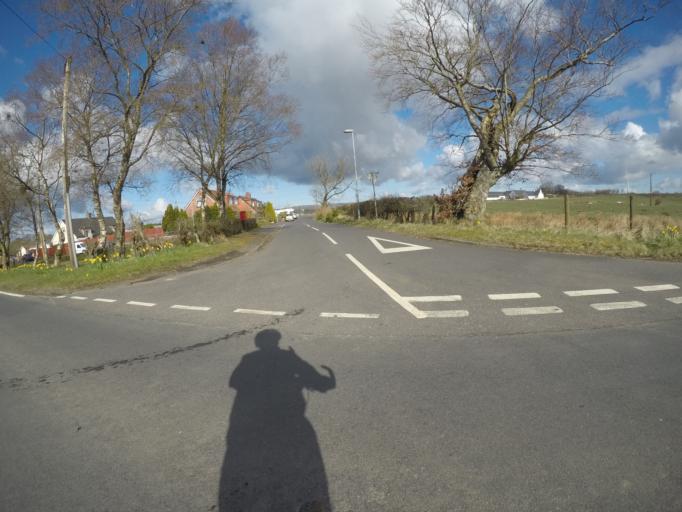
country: GB
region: Scotland
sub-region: North Ayrshire
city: Kilwinning
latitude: 55.6732
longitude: -4.6584
